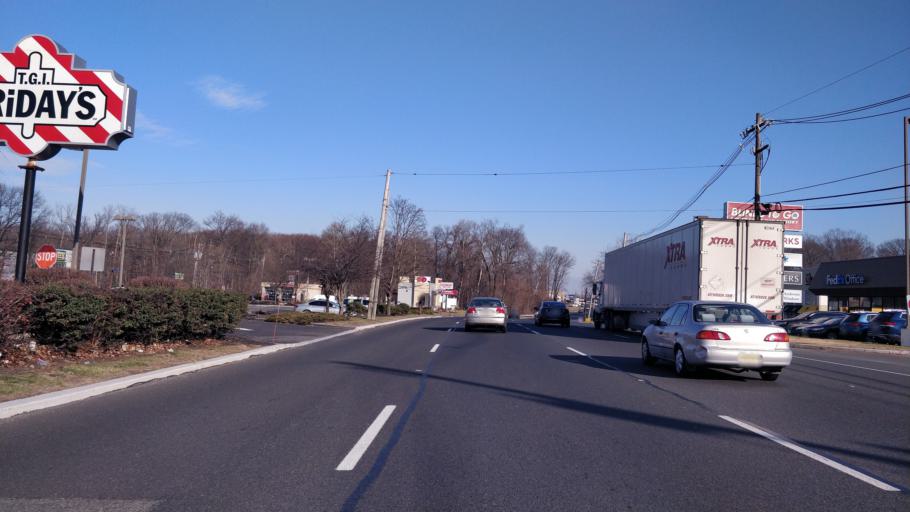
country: US
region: New Jersey
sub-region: Union County
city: Springfield
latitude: 40.6873
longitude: -74.3144
